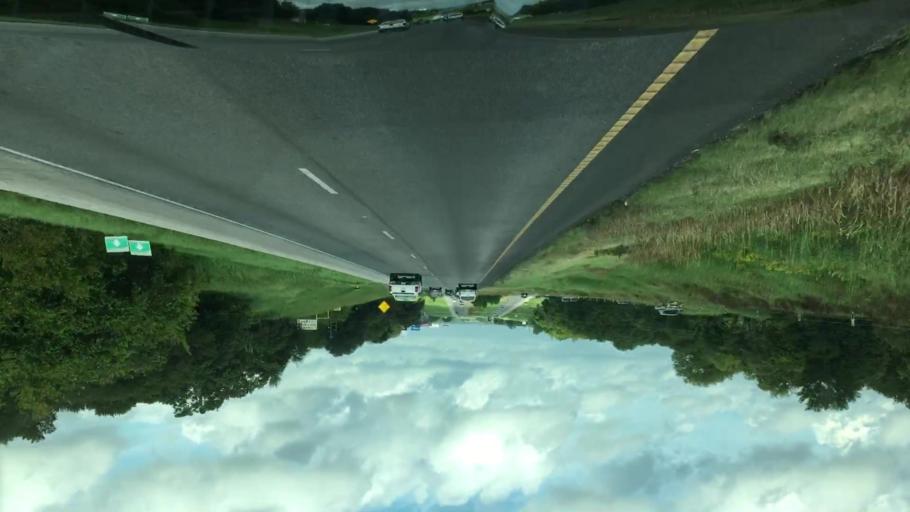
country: US
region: Texas
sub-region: Bastrop County
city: Wyldwood
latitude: 30.1546
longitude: -97.4934
